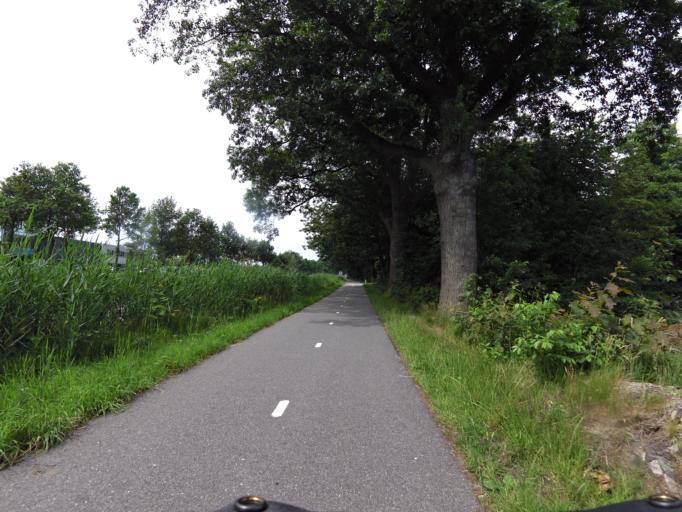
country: NL
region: Gelderland
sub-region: Gemeente Apeldoorn
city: Beekbergen
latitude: 52.1621
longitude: 6.0058
